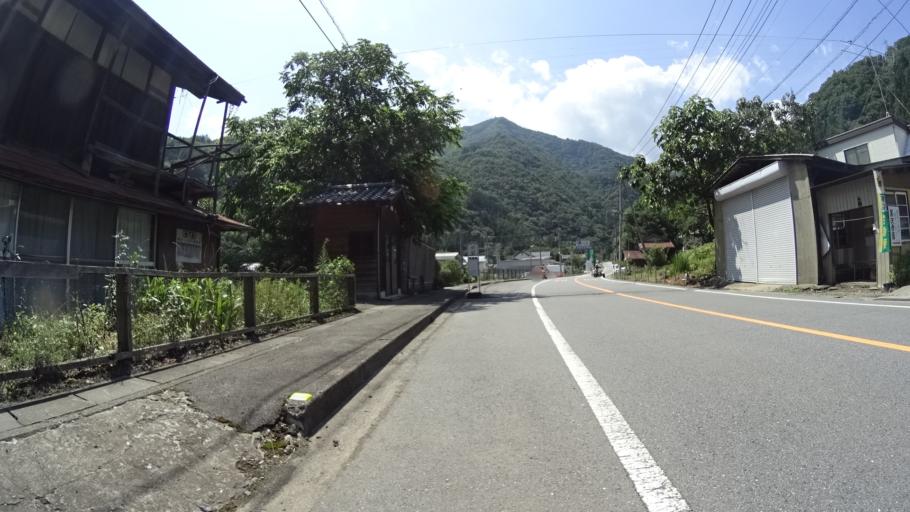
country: JP
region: Gunma
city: Tomioka
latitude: 36.0820
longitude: 138.7841
